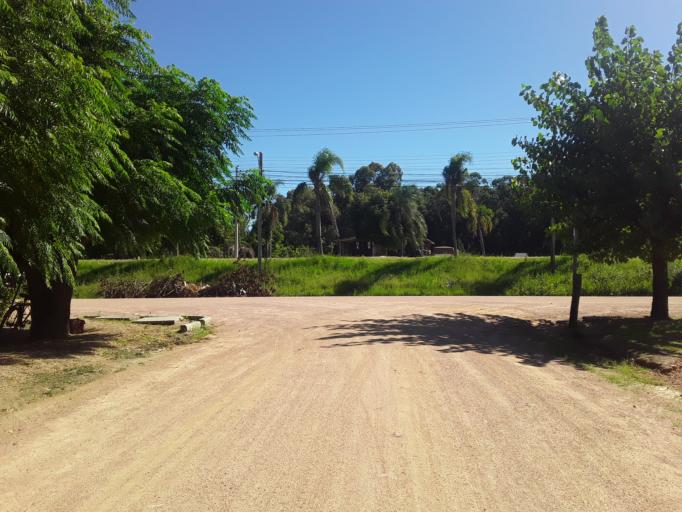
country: BR
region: Rio Grande do Sul
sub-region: Sao Lourenco Do Sul
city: Sao Lourenco do Sul
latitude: -31.3459
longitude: -51.9941
